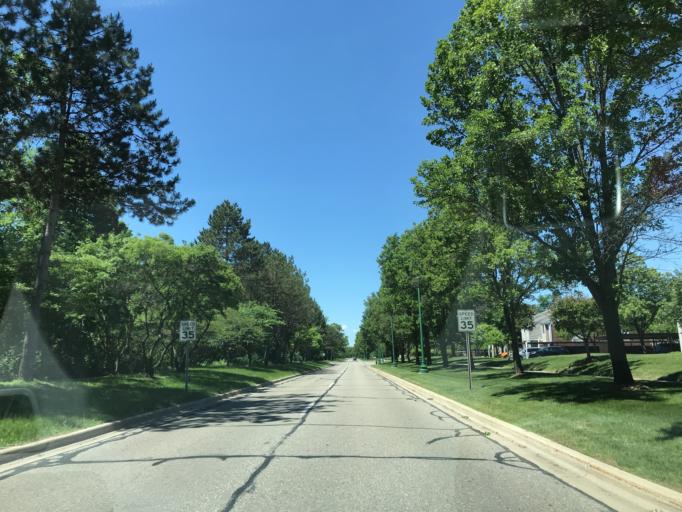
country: US
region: Michigan
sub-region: Oakland County
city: Bingham Farms
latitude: 42.4793
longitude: -83.2706
